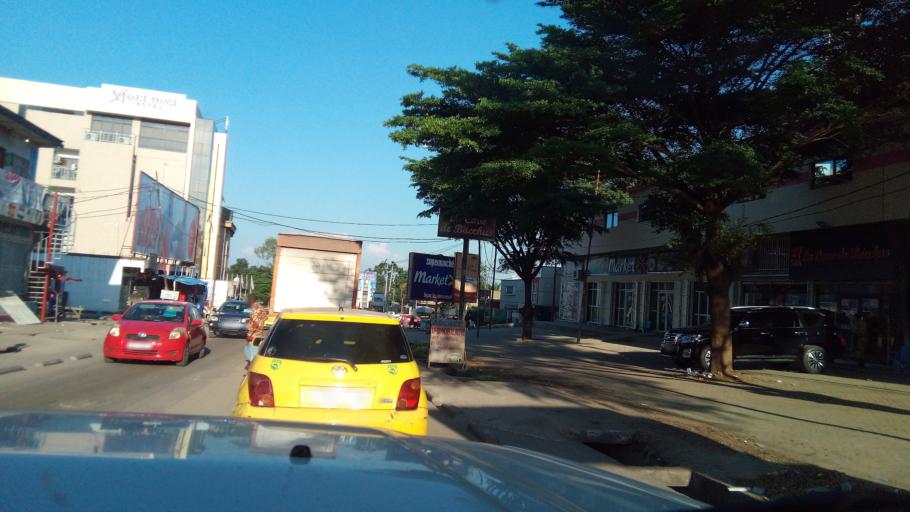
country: CD
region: Kinshasa
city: Kinshasa
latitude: -4.3461
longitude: 15.2658
